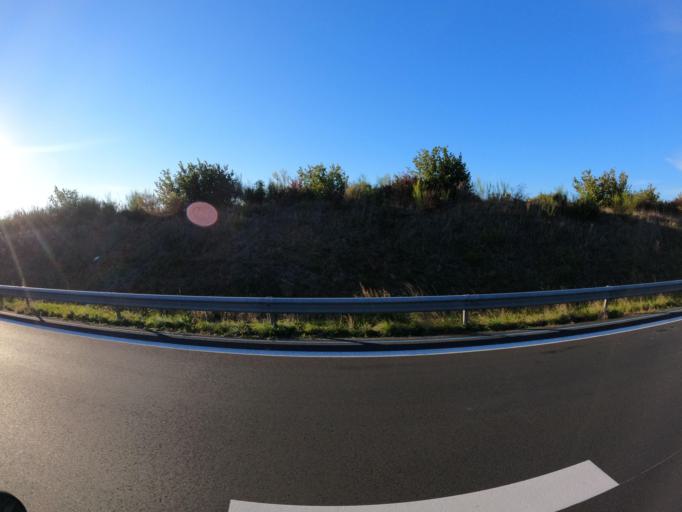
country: FR
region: Pays de la Loire
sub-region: Departement de la Vendee
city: La Gaubretiere
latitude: 46.9054
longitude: -1.0516
